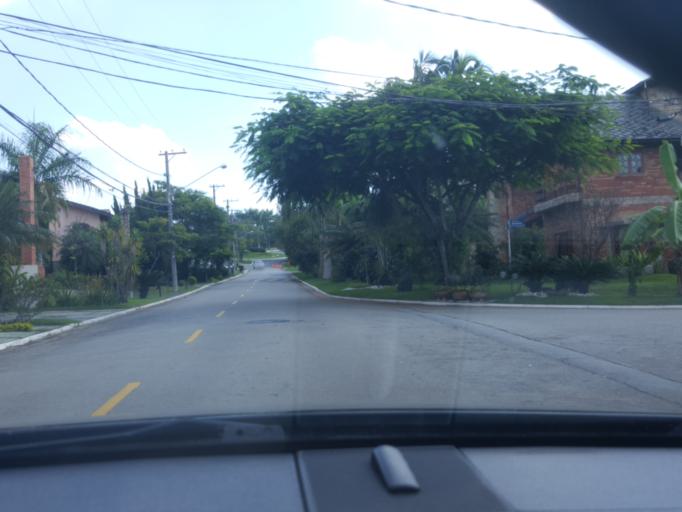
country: BR
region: Sao Paulo
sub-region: Carapicuiba
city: Carapicuiba
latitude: -23.4848
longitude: -46.8368
